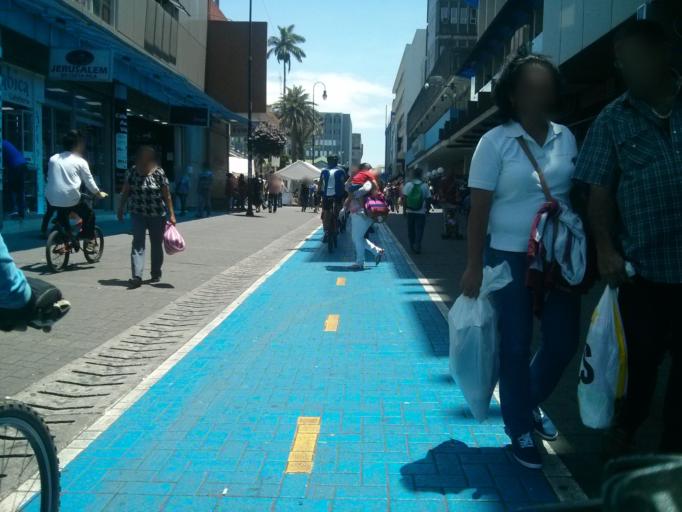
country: CR
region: San Jose
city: San Jose
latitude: 9.9325
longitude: -84.0805
